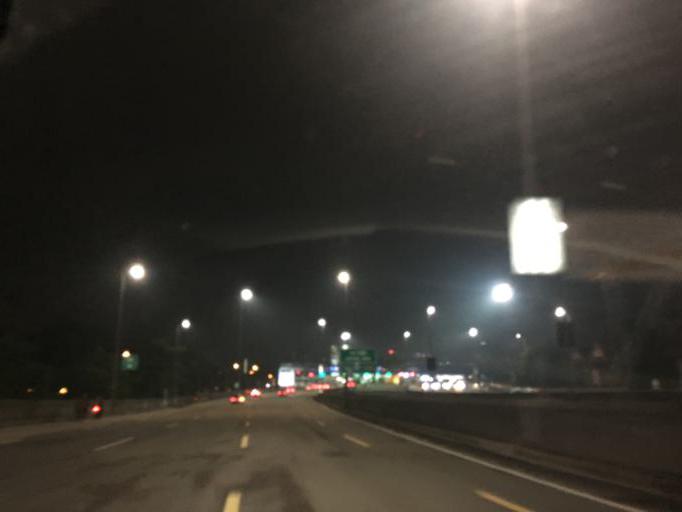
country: MY
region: Kuala Lumpur
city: Kuala Lumpur
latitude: 3.1662
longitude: 101.7189
